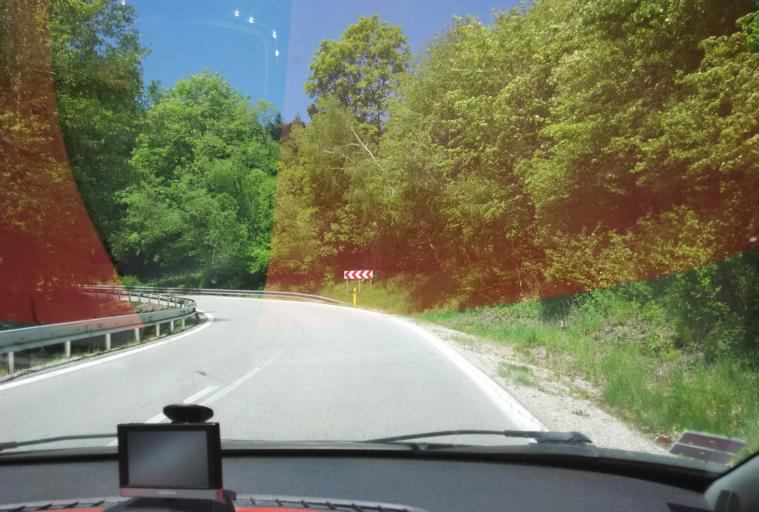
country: SK
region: Kosicky
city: Dobsina
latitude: 48.8423
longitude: 20.3841
